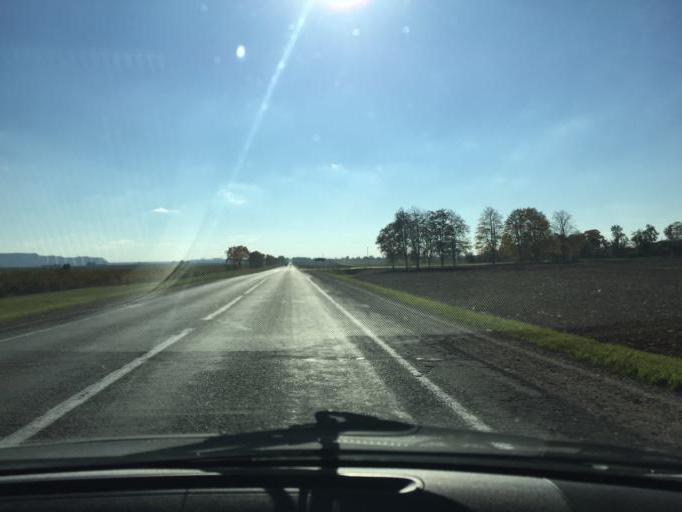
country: BY
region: Minsk
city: Slutsk
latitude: 52.9376
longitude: 27.4894
